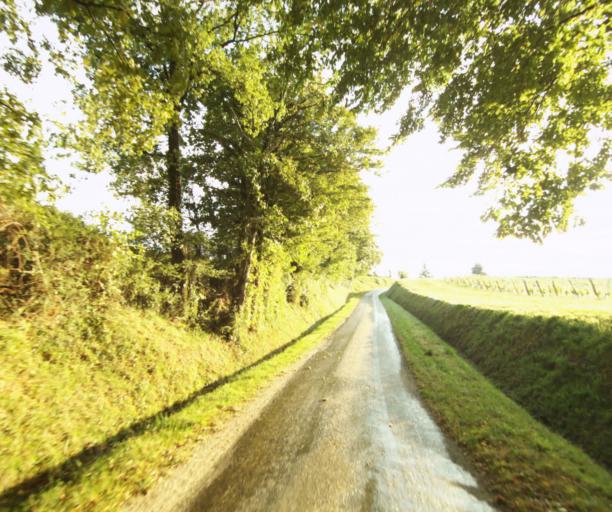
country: FR
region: Midi-Pyrenees
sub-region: Departement du Gers
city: Cazaubon
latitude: 43.9212
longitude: -0.0373
